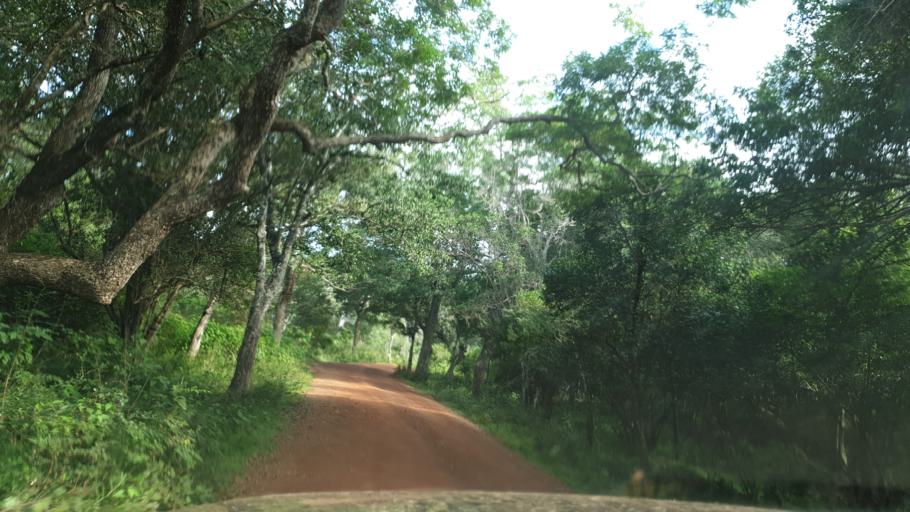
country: LK
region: North Central
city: Anuradhapura
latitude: 8.3786
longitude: 80.0690
